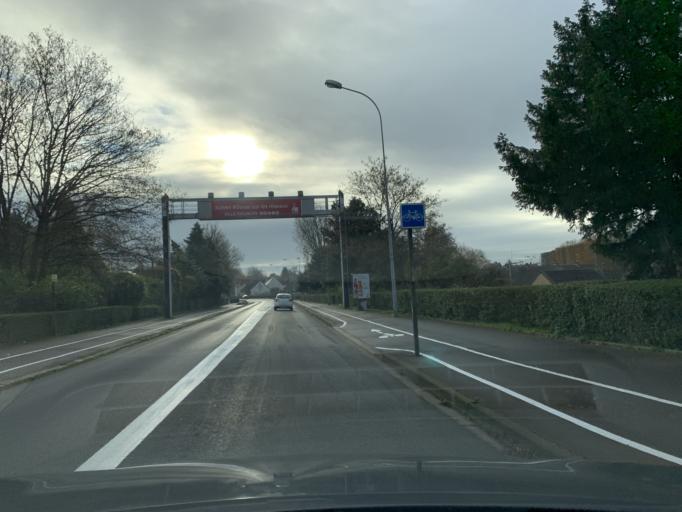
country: FR
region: Nord-Pas-de-Calais
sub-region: Departement du Nord
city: Lambres-lez-Douai
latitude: 50.3559
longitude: 3.0820
